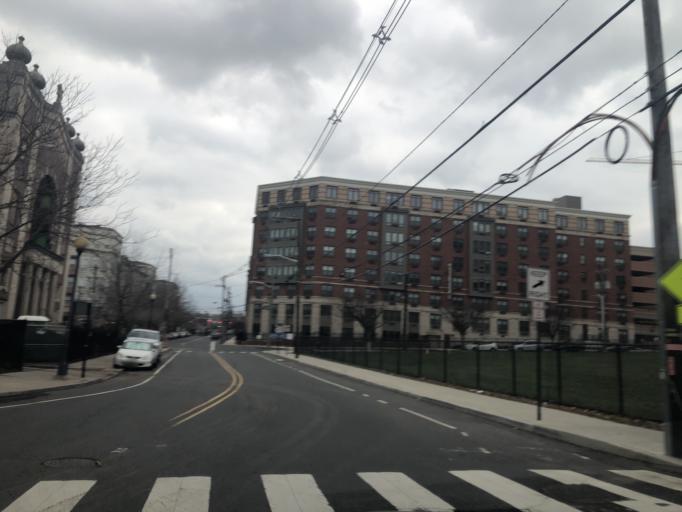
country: US
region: New Jersey
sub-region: Middlesex County
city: New Brunswick
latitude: 40.4947
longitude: -74.4419
